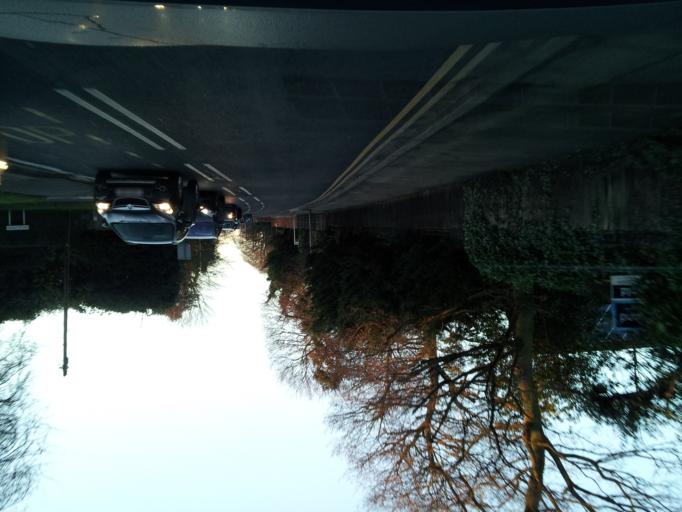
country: GB
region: England
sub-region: Essex
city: Chelmsford
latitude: 51.7402
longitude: 0.4901
